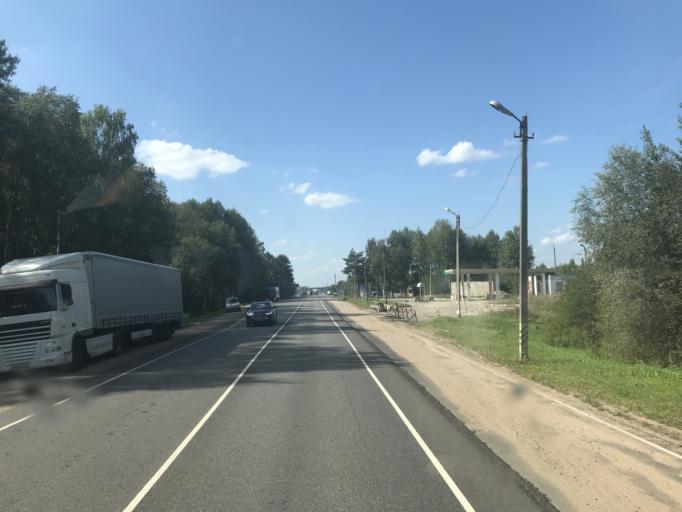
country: RU
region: Smolensk
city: Rudnya
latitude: 54.9857
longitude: 30.9625
